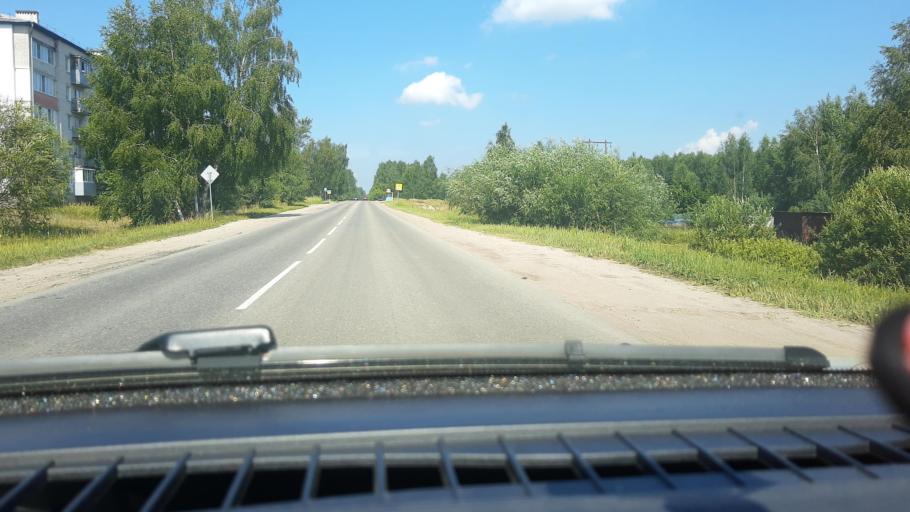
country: RU
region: Nizjnij Novgorod
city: Afonino
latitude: 56.3036
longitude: 44.1832
